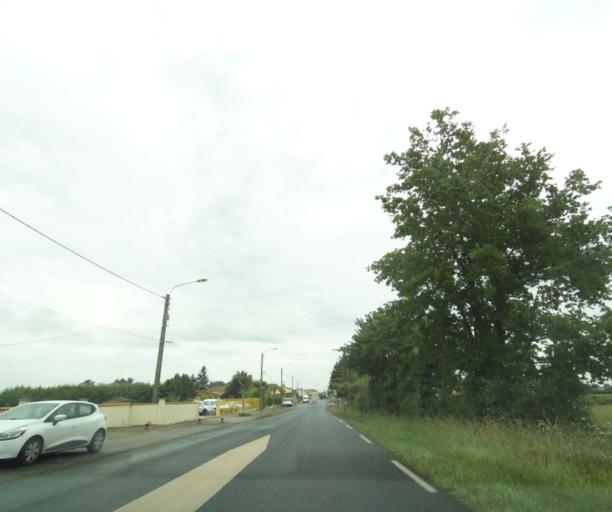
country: FR
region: Poitou-Charentes
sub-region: Departement des Deux-Sevres
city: Viennay
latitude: 46.7276
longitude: -0.2375
